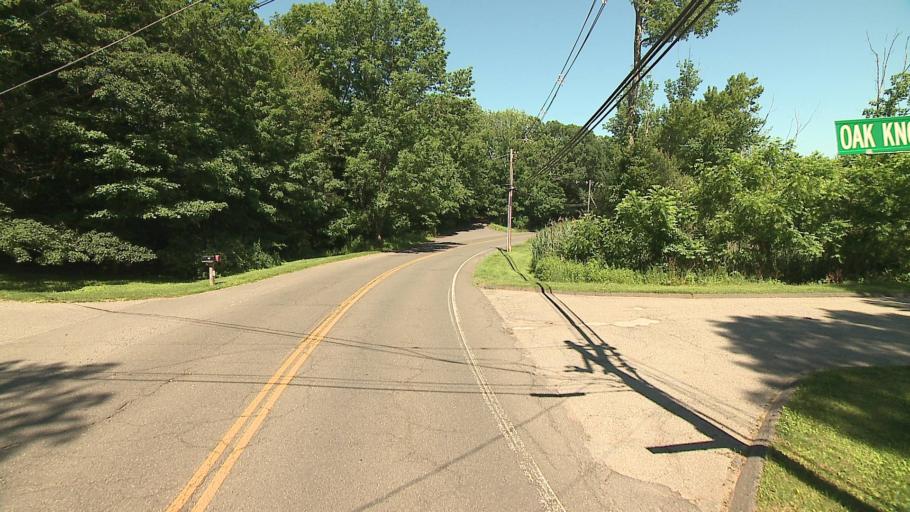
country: US
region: Connecticut
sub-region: Fairfield County
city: Ridgefield
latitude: 41.2849
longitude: -73.5169
